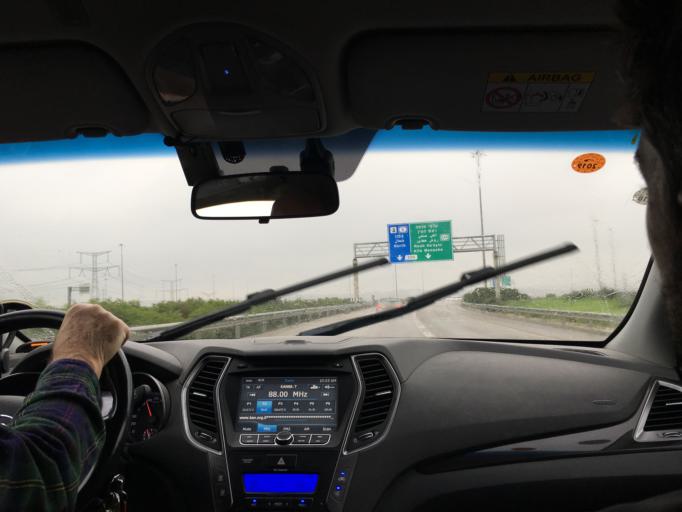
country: IL
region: Central District
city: Rosh Ha'Ayin
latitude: 32.1158
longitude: 34.9327
